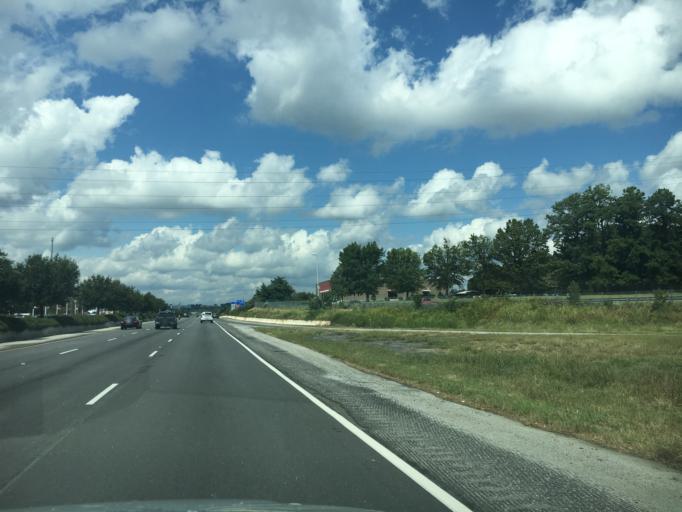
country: US
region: South Carolina
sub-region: Greenville County
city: Mauldin
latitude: 34.8409
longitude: -82.3153
